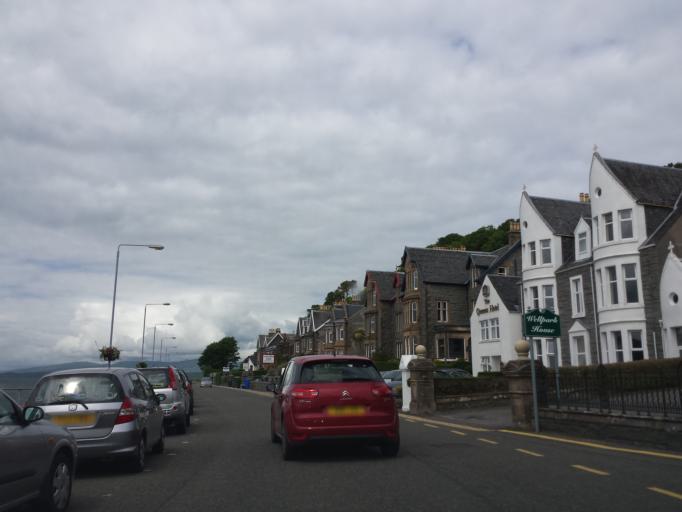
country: GB
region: Scotland
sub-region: Argyll and Bute
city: Oban
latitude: 56.4205
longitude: -5.4813
